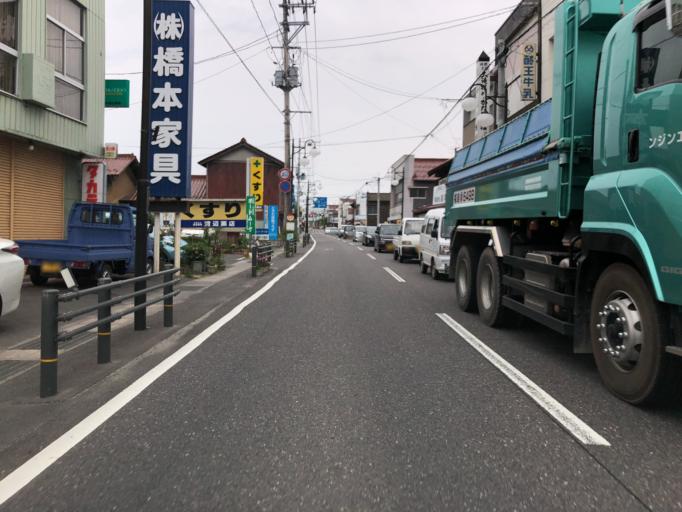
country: JP
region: Fukushima
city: Funehikimachi-funehiki
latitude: 37.4386
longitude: 140.5745
